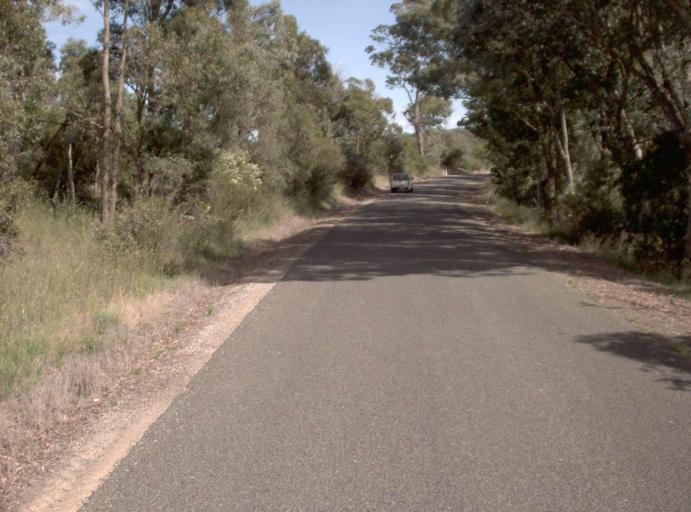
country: AU
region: Victoria
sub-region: East Gippsland
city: Lakes Entrance
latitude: -37.4933
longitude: 148.1316
